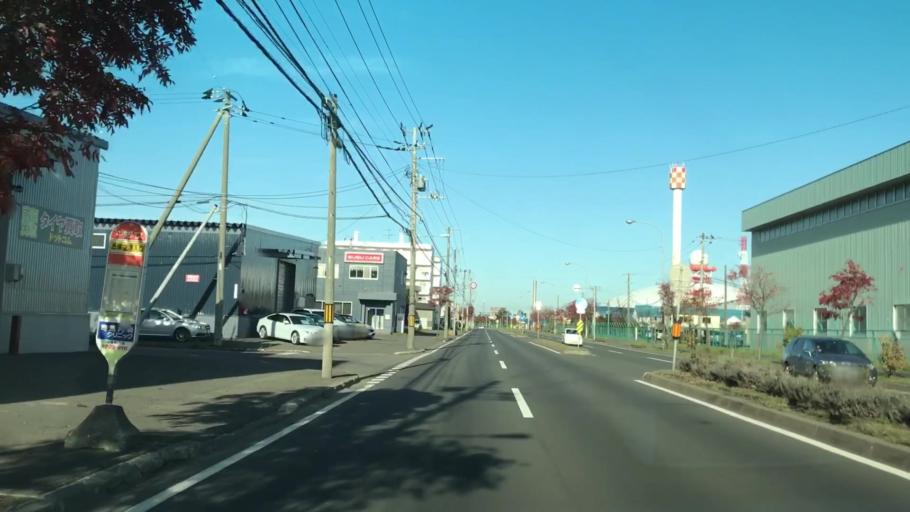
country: JP
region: Hokkaido
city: Sapporo
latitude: 43.1106
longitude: 141.3797
